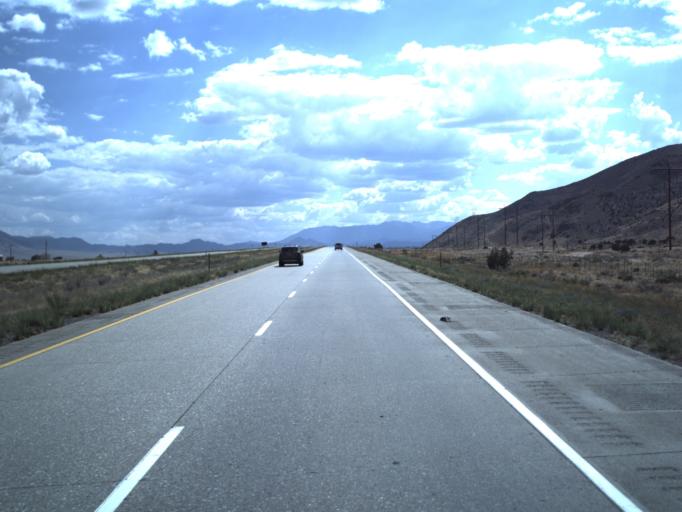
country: US
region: Utah
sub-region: Sevier County
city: Richfield
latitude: 38.7164
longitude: -112.1345
